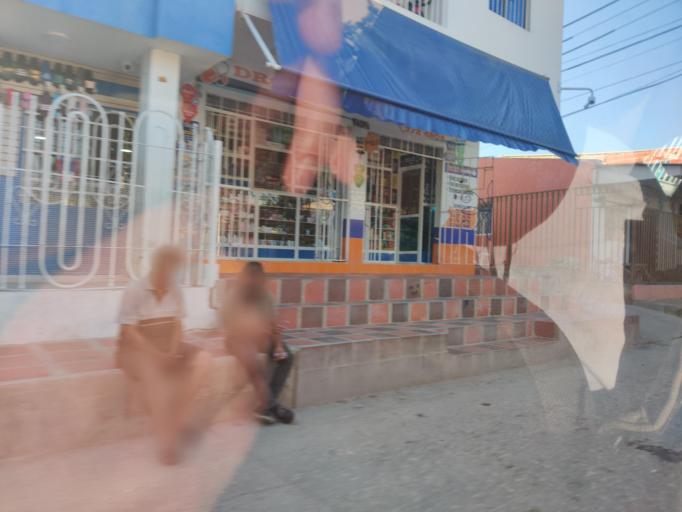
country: CO
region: Atlantico
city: Soledad
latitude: 10.9137
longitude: -74.8021
